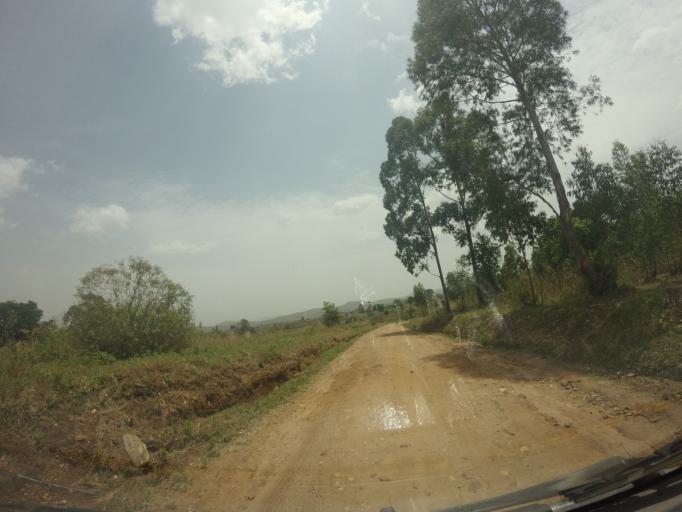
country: UG
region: Northern Region
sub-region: Arua District
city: Arua
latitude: 2.9355
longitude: 30.9159
